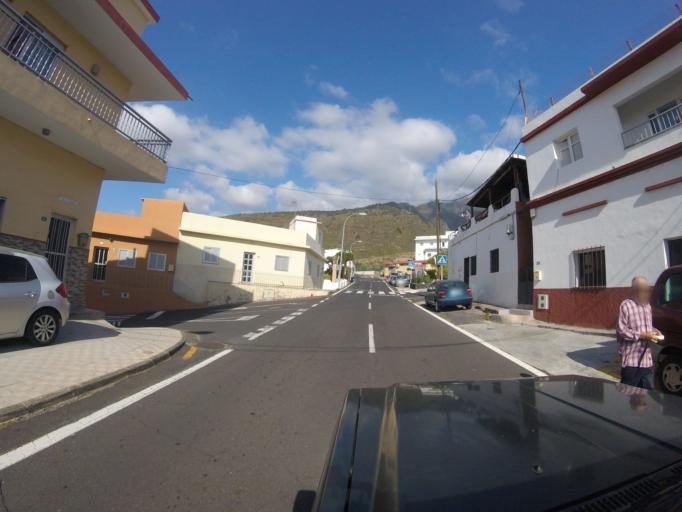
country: ES
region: Canary Islands
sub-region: Provincia de Santa Cruz de Tenerife
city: Candelaria
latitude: 28.3790
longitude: -16.3722
